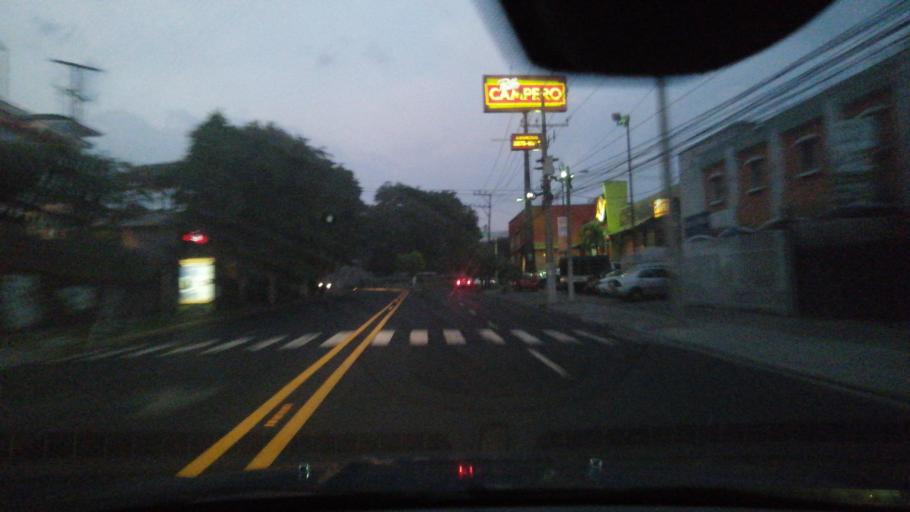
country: SV
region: San Salvador
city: San Salvador
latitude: 13.7094
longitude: -89.2039
